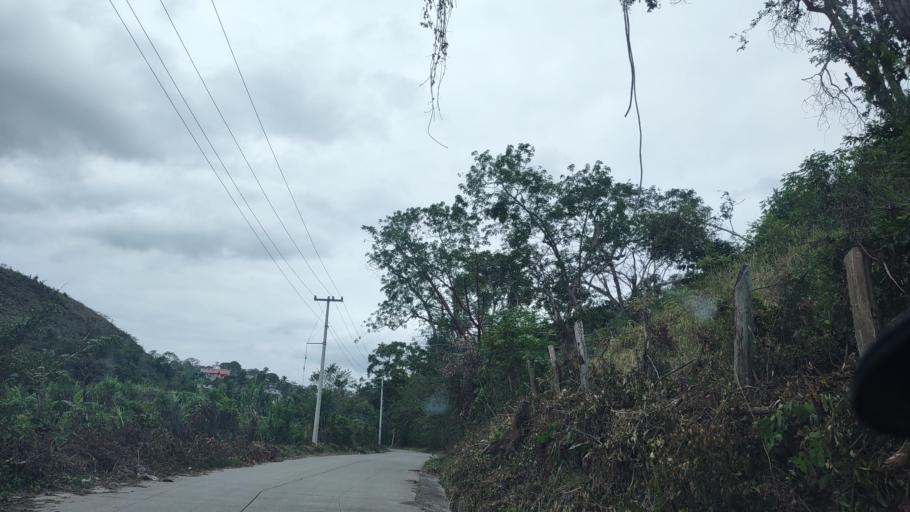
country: MX
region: Veracruz
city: Papantla de Olarte
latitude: 20.4424
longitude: -97.3016
